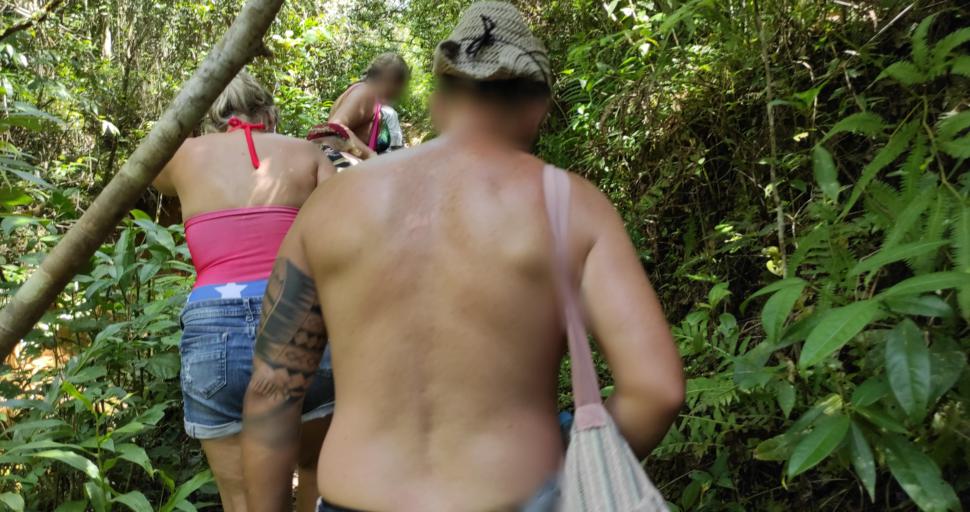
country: BR
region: Santa Catarina
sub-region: Porto Belo
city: Porto Belo
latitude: -27.1946
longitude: -48.5588
